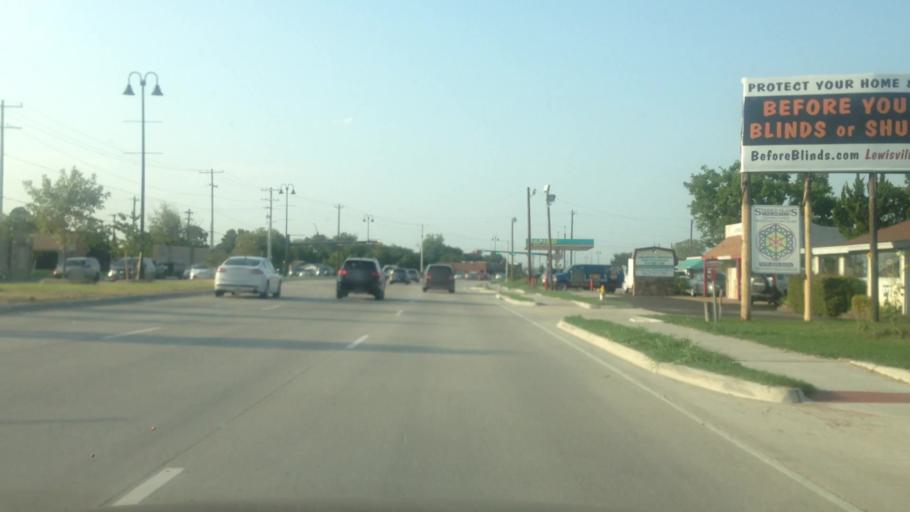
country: US
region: Texas
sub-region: Denton County
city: The Colony
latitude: 33.1014
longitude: -96.8924
